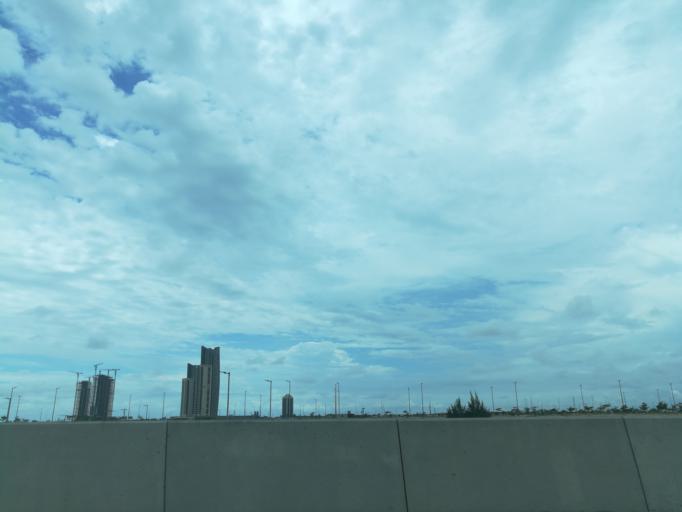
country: NG
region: Lagos
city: Ikoyi
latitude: 6.4145
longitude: 3.4179
